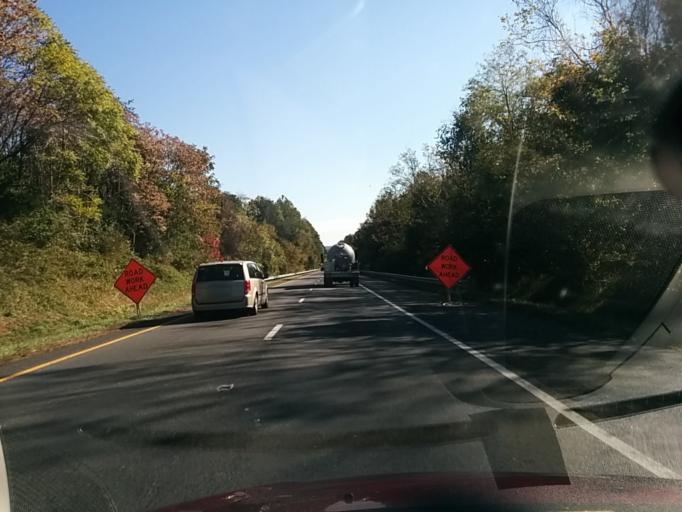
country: US
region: Virginia
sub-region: Albemarle County
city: Crozet
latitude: 38.0329
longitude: -78.6352
